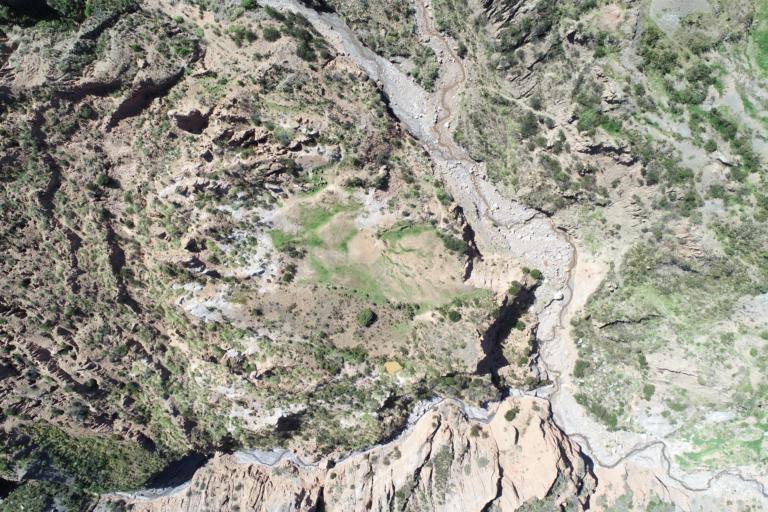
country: BO
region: La Paz
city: La Paz
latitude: -16.5578
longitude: -67.9909
